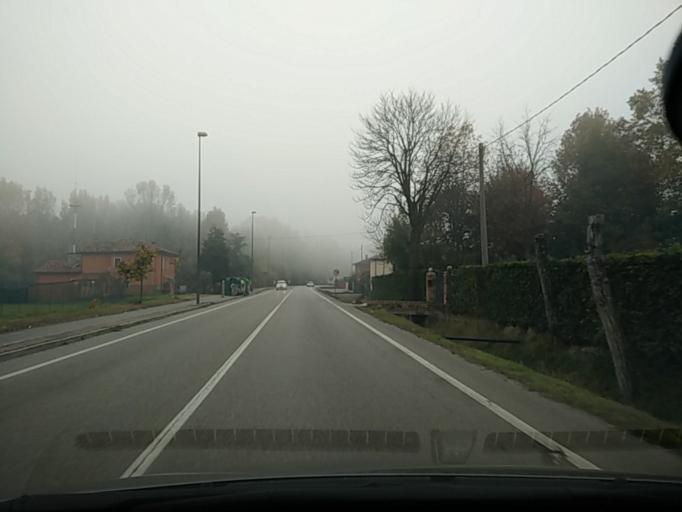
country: IT
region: Veneto
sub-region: Provincia di Venezia
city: Mirano
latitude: 45.5092
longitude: 12.1126
